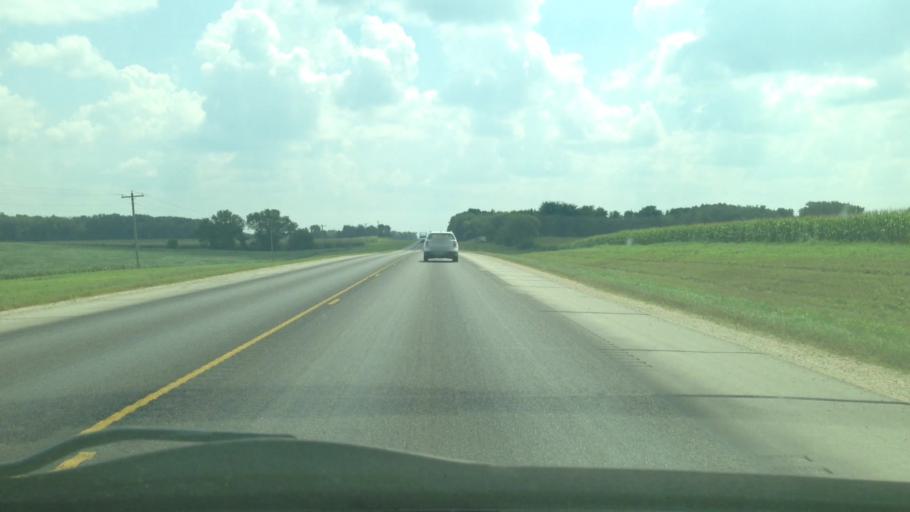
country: US
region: Minnesota
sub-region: Mower County
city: Grand Meadow
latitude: 43.7358
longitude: -92.4793
